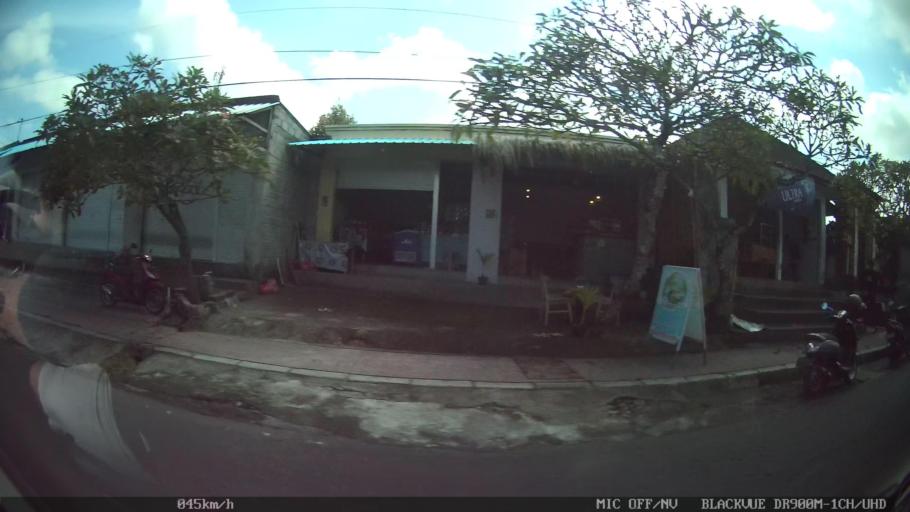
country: ID
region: Bali
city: Banjar Kelodan
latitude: -8.5339
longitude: 115.3287
